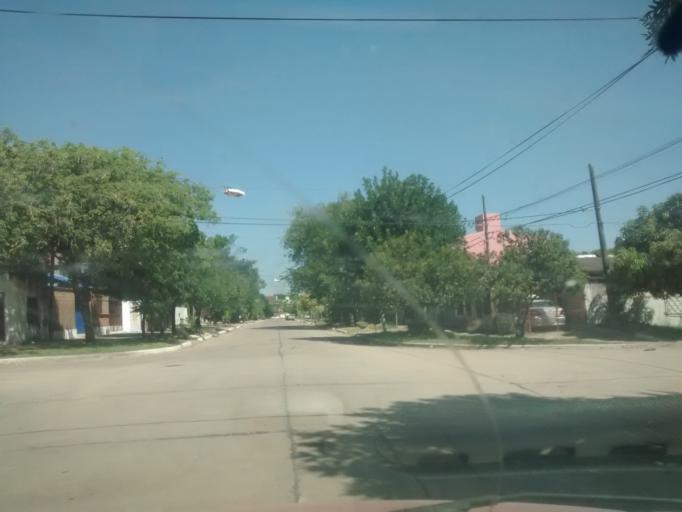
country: AR
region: Chaco
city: Resistencia
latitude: -27.4595
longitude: -58.9996
